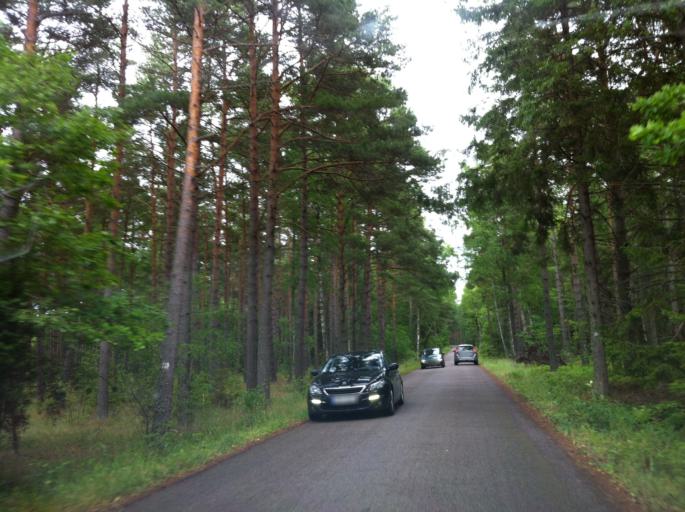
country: SE
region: Kalmar
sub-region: Vasterviks Kommun
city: Vaestervik
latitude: 57.3326
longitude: 17.1022
